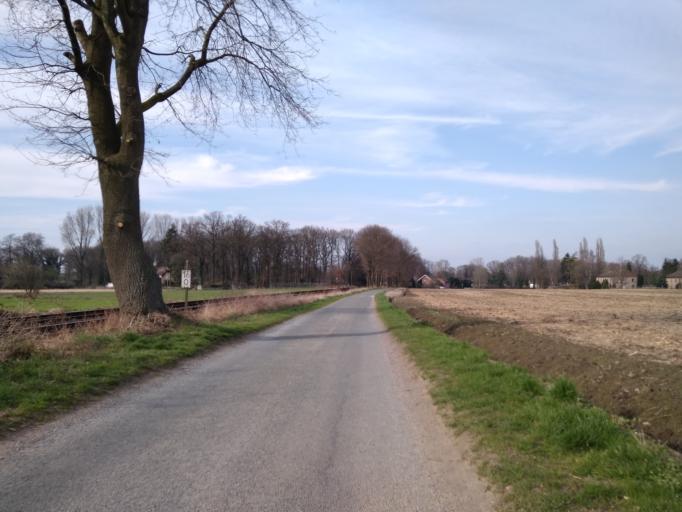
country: DE
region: North Rhine-Westphalia
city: Dorsten
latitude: 51.6318
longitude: 6.9688
